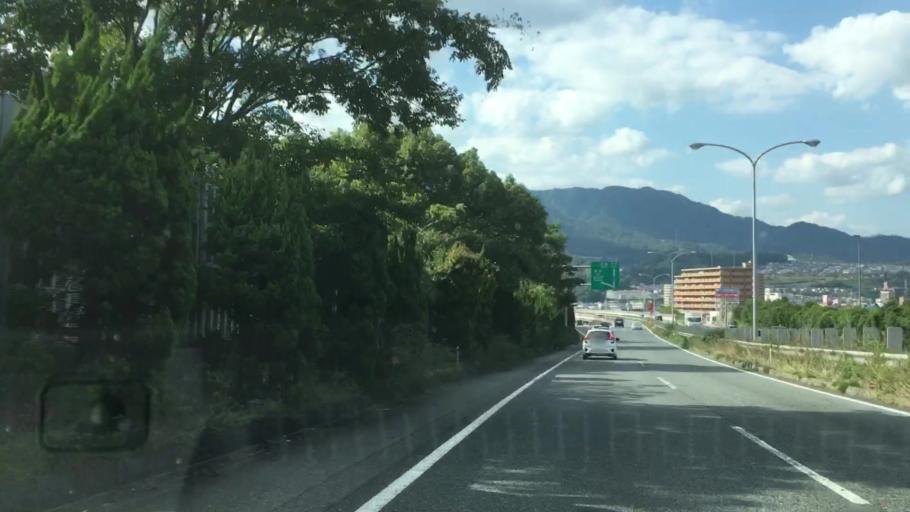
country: JP
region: Hiroshima
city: Hatsukaichi
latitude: 34.3773
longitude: 132.3667
